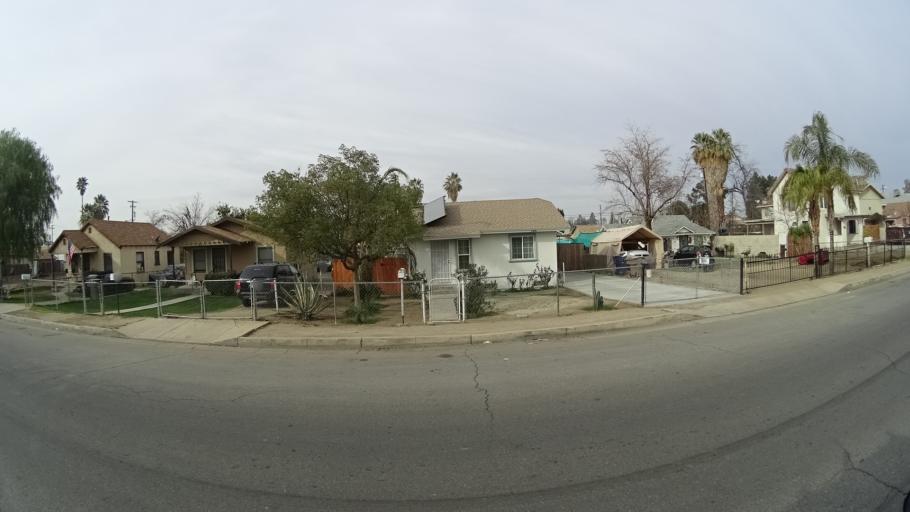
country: US
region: California
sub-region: Kern County
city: Bakersfield
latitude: 35.3560
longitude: -119.0165
